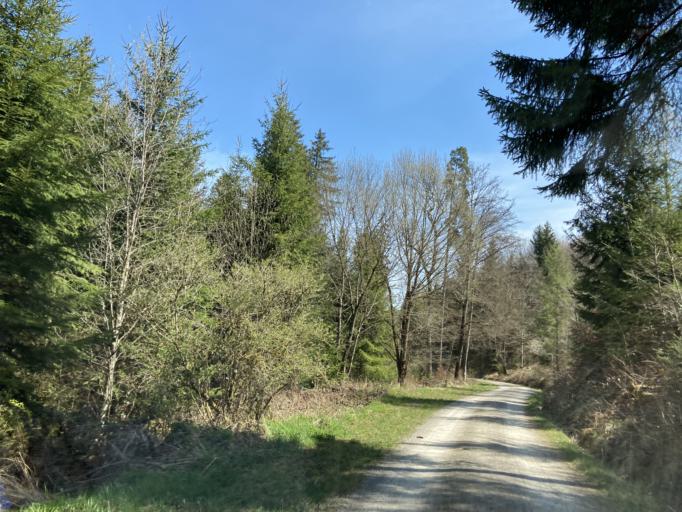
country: DE
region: Baden-Wuerttemberg
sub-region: Tuebingen Region
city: Tuebingen
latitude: 48.5533
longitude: 9.0437
